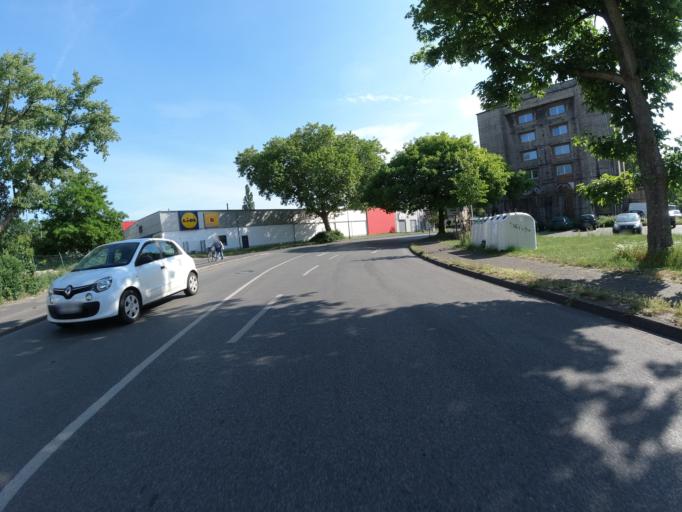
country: DE
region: North Rhine-Westphalia
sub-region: Regierungsbezirk Dusseldorf
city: Hochfeld
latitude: 51.4035
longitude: 6.7239
